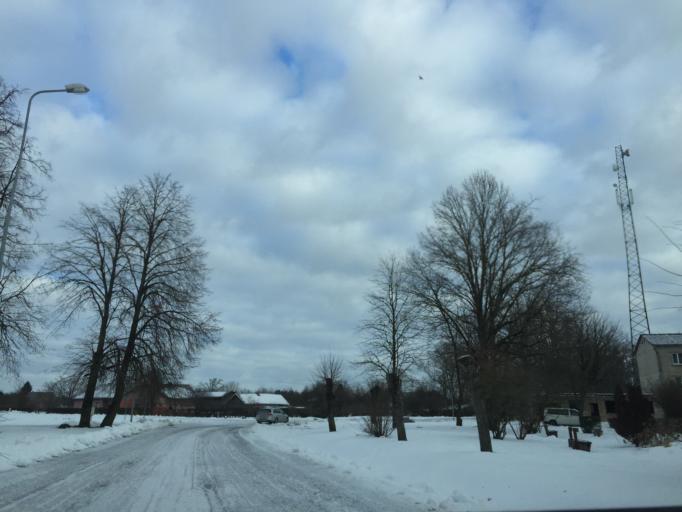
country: LV
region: Lielvarde
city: Lielvarde
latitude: 56.6308
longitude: 24.7517
